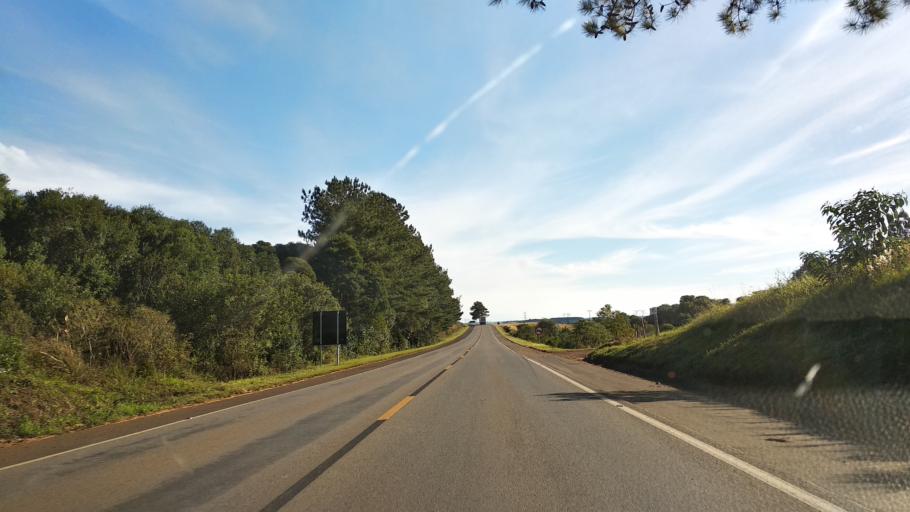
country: BR
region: Santa Catarina
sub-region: Celso Ramos
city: Celso Ramos
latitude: -27.5315
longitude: -51.3934
